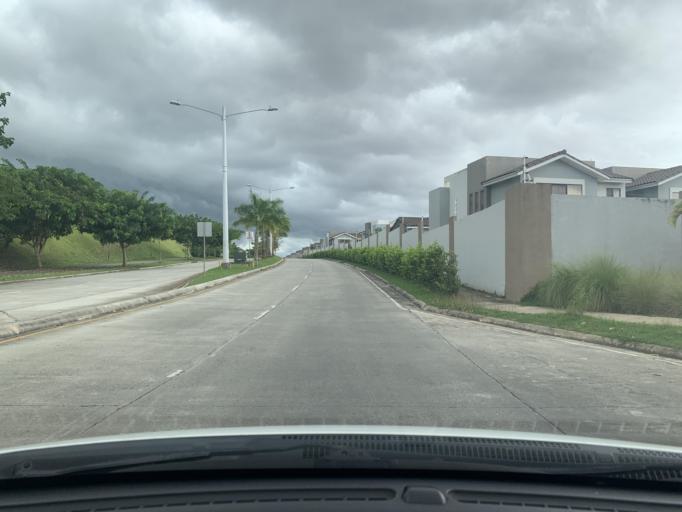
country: PA
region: Panama
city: San Miguelito
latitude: 9.0900
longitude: -79.4673
